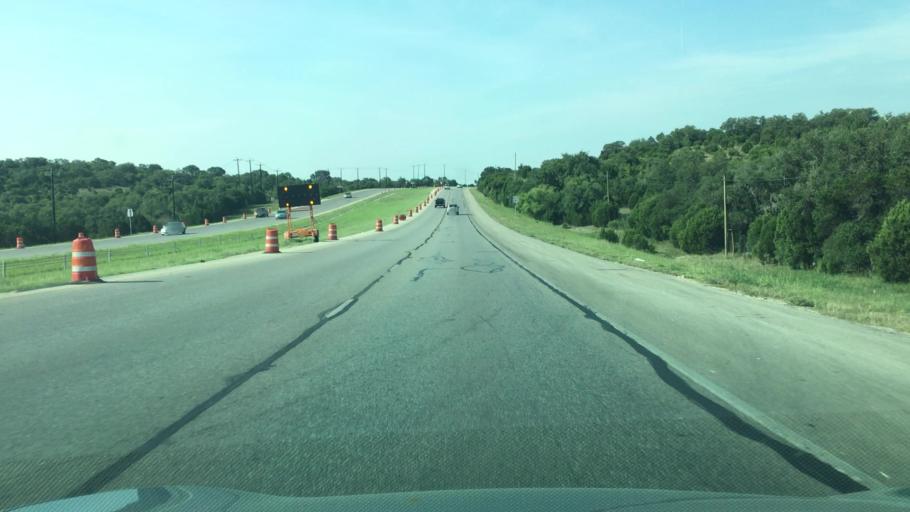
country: US
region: Texas
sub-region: Comal County
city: Bulverde
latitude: 29.7707
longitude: -98.4278
